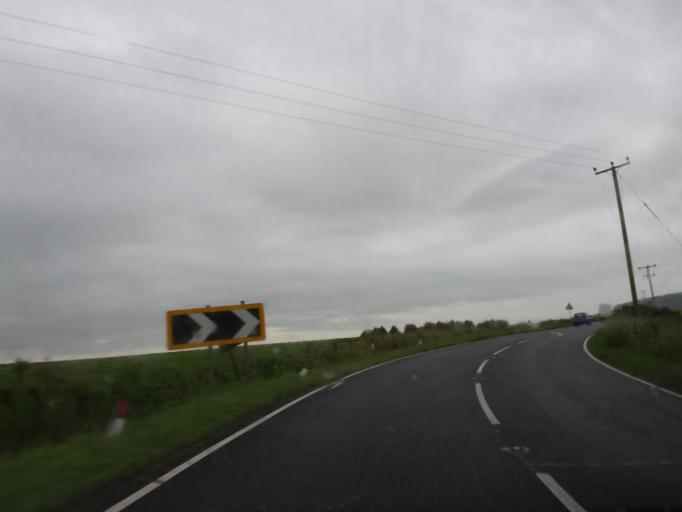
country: GB
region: Scotland
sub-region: Fife
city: Balmullo
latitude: 56.4081
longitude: -2.9134
